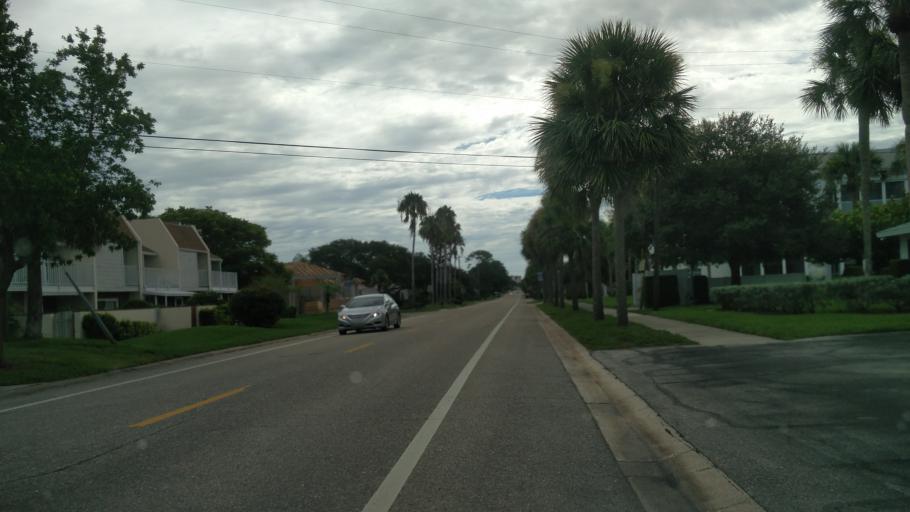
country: US
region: Florida
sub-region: Sarasota County
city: Venice
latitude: 27.1011
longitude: -82.4591
